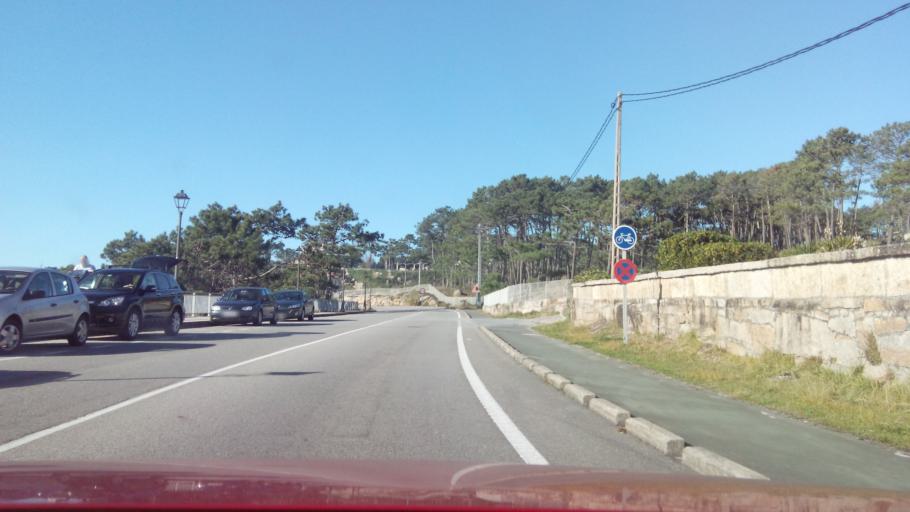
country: ES
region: Galicia
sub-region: Provincia de Pontevedra
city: O Grove
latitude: 42.4578
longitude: -8.8848
